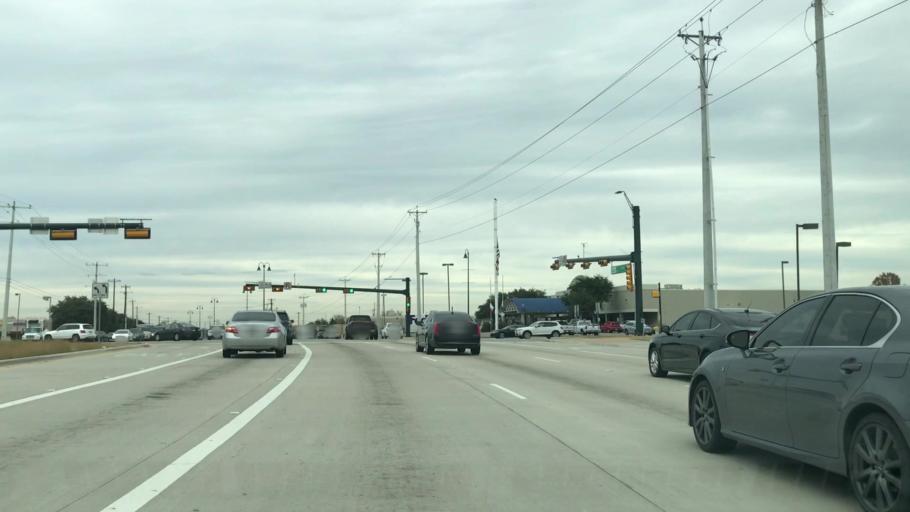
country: US
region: Texas
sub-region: Denton County
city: The Colony
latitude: 33.0958
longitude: -96.8924
